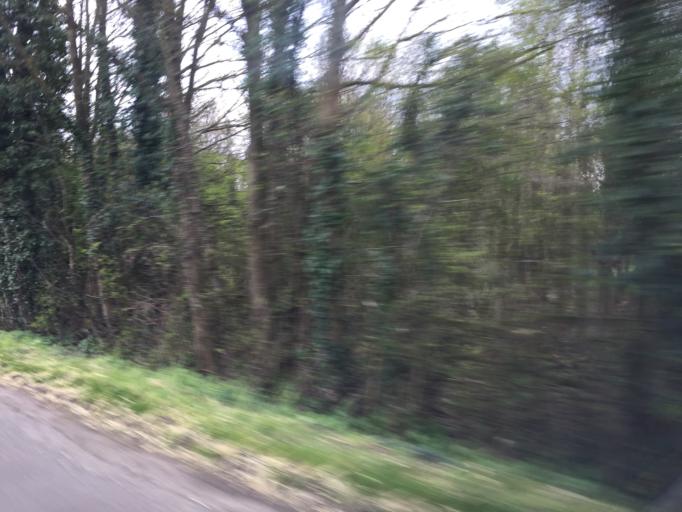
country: GB
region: England
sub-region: Oxfordshire
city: Bicester
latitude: 51.9384
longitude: -1.1314
